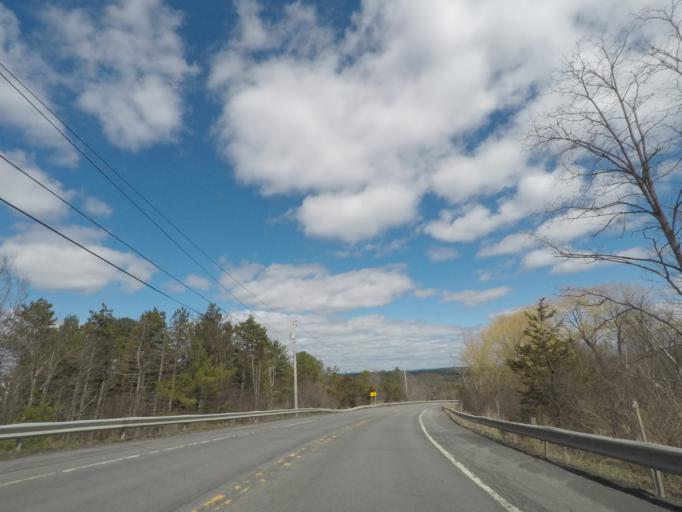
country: US
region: New York
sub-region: Albany County
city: Voorheesville
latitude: 42.6239
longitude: -73.9743
